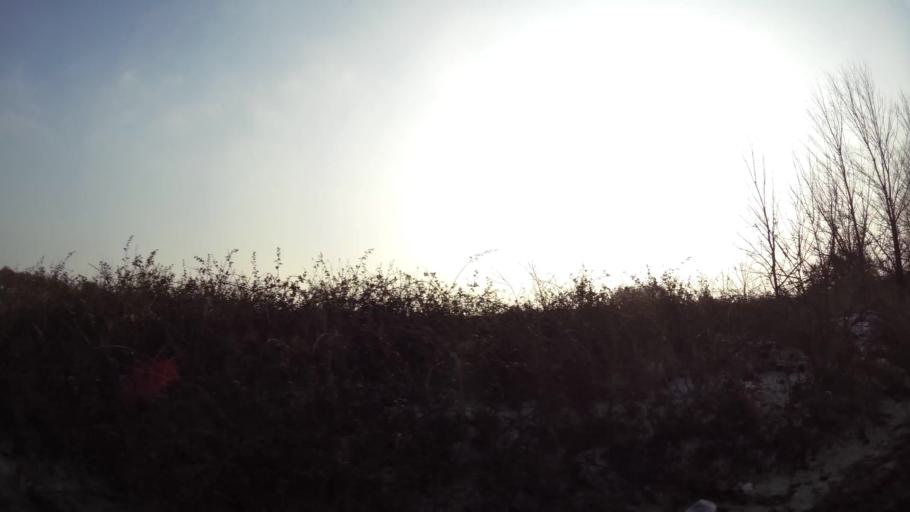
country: MK
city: Kadino
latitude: 41.9777
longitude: 21.6239
